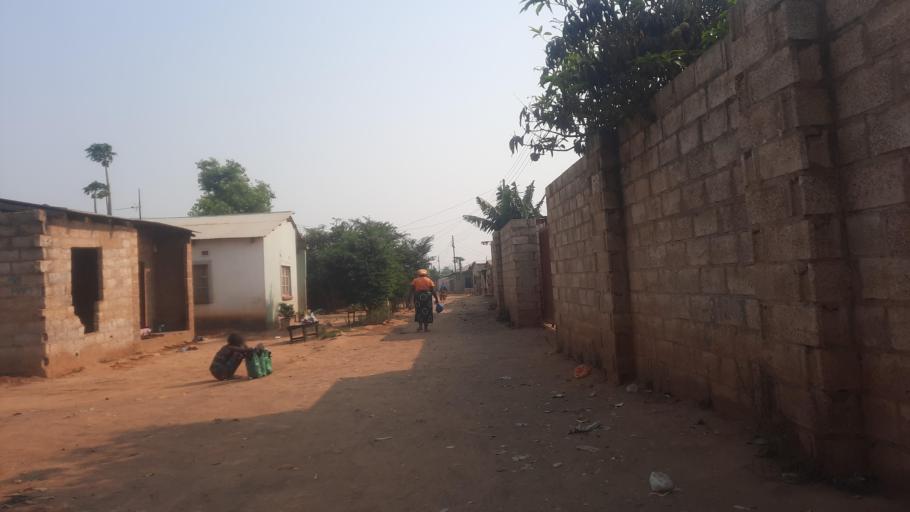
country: ZM
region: Lusaka
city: Lusaka
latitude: -15.3963
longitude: 28.3830
